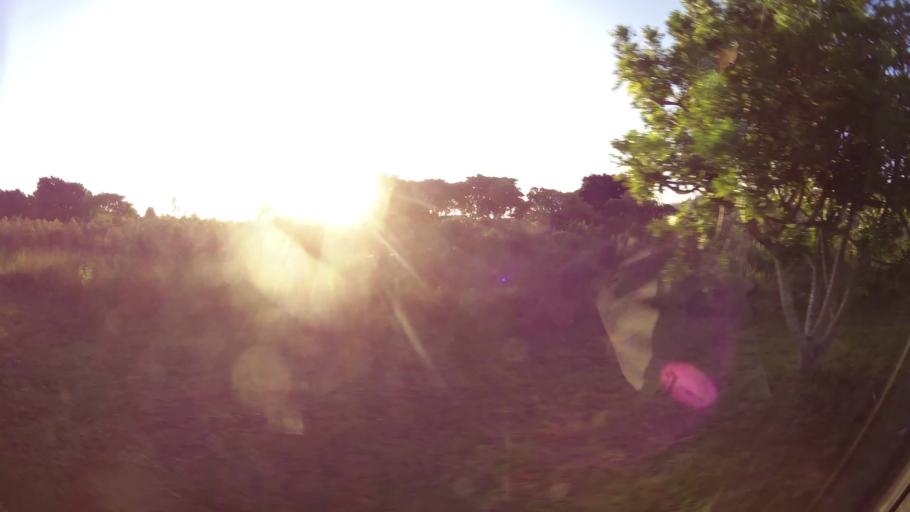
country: ZA
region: Western Cape
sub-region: Eden District Municipality
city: Knysna
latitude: -34.0154
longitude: 22.7866
